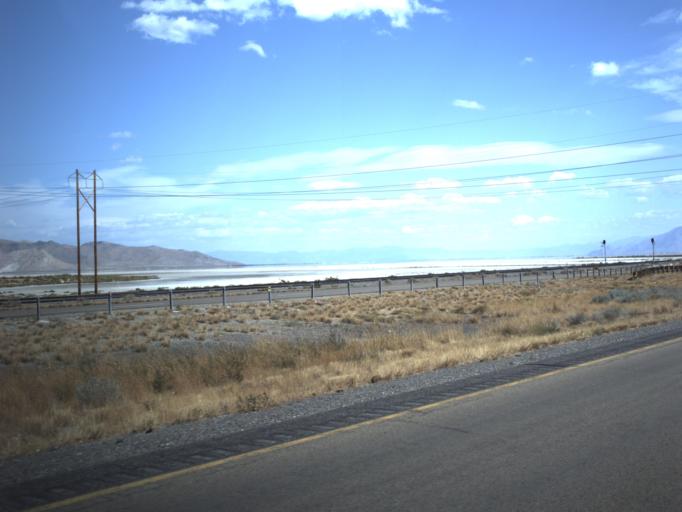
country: US
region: Utah
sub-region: Tooele County
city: Grantsville
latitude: 40.7430
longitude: -112.6326
